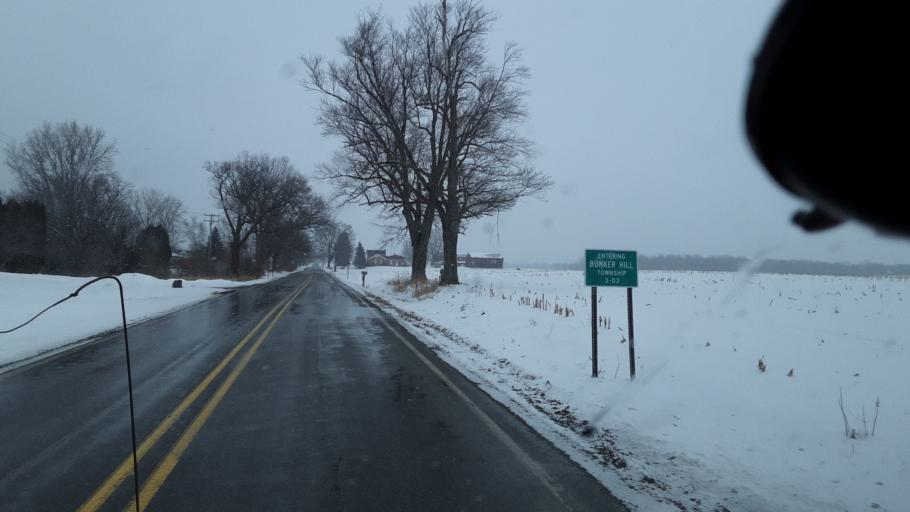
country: US
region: Michigan
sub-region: Ingham County
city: Leslie
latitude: 42.4252
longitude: -84.3168
